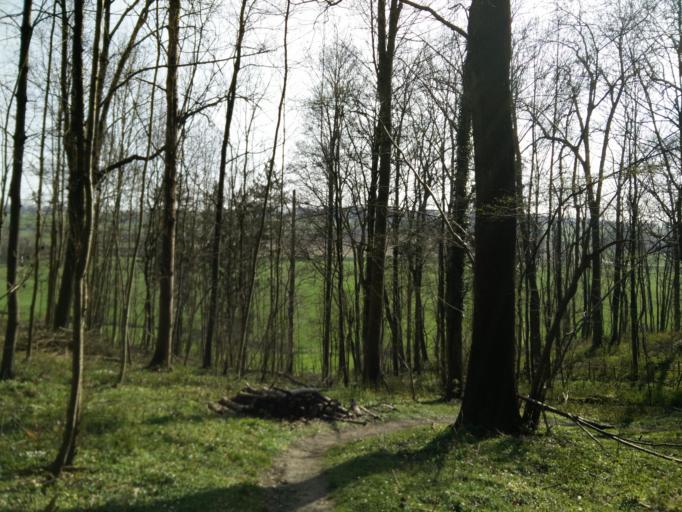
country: BE
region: Flanders
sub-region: Provincie Limburg
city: Sint-Pieters-Voeren
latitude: 50.7539
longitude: 5.7981
